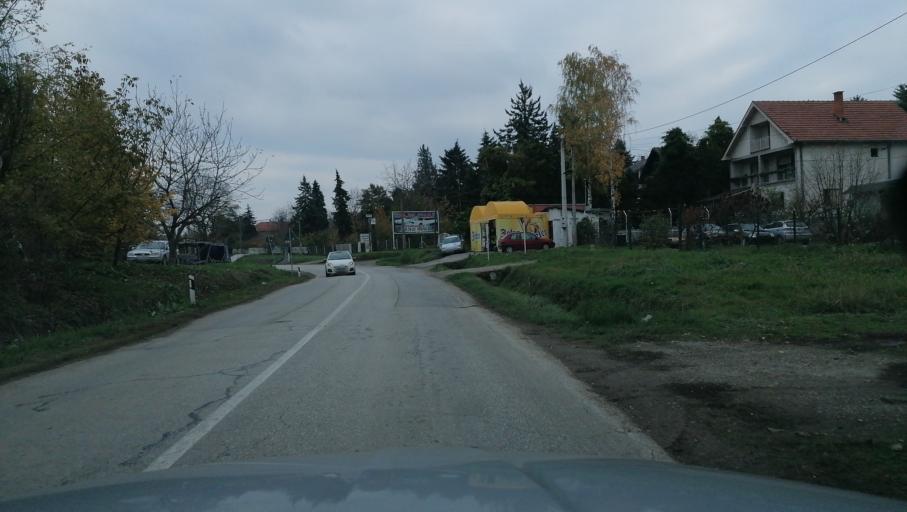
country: RS
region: Central Serbia
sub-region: Podunavski Okrug
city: Smederevo
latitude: 44.6568
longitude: 20.8701
